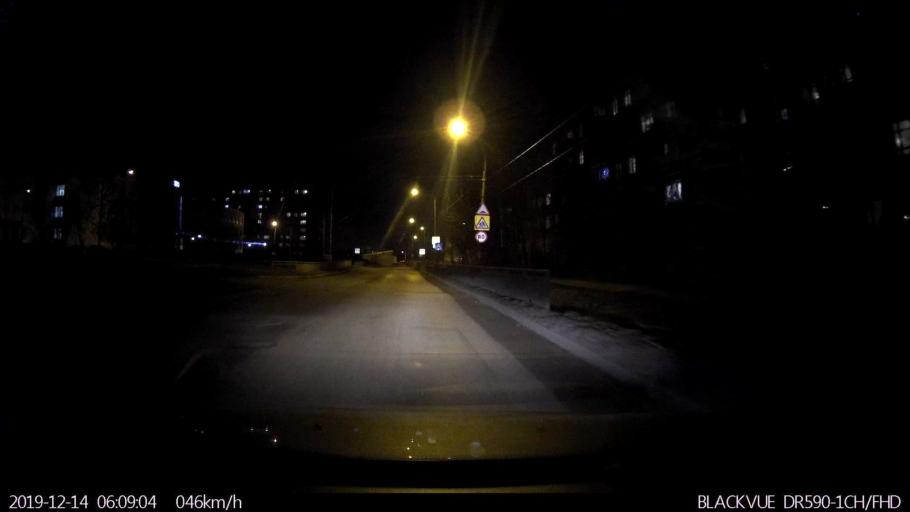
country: RU
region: Nizjnij Novgorod
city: Gorbatovka
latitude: 56.2674
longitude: 43.8700
